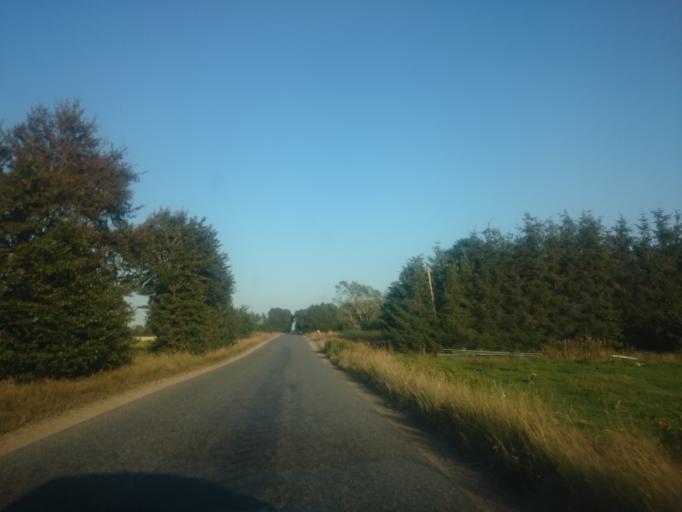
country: DK
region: South Denmark
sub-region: Billund Kommune
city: Billund
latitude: 55.7408
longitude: 9.0299
